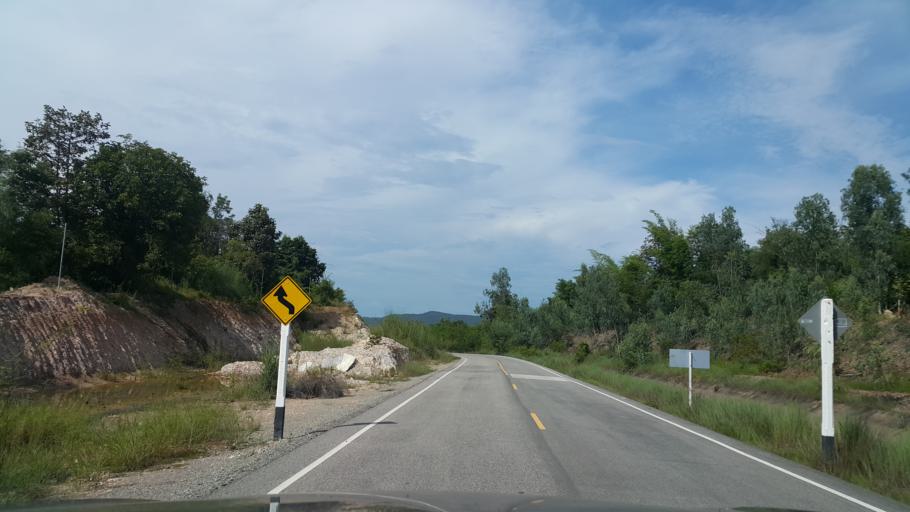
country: TH
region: Chiang Mai
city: Mae On
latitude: 18.8142
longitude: 99.1806
